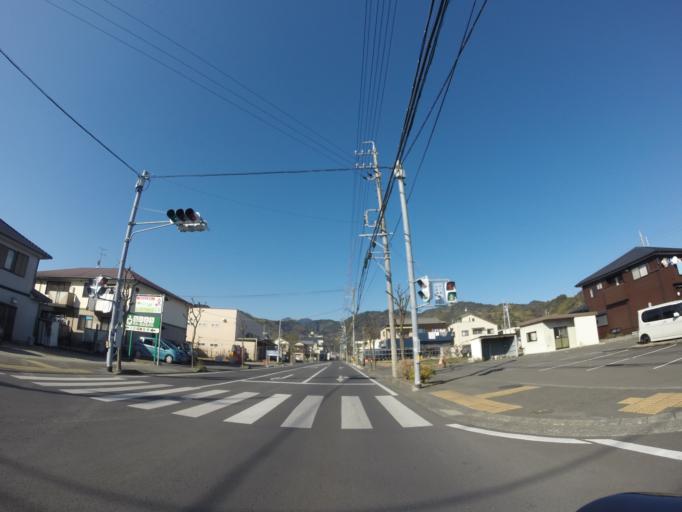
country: JP
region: Shizuoka
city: Shizuoka-shi
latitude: 35.0364
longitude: 138.4562
